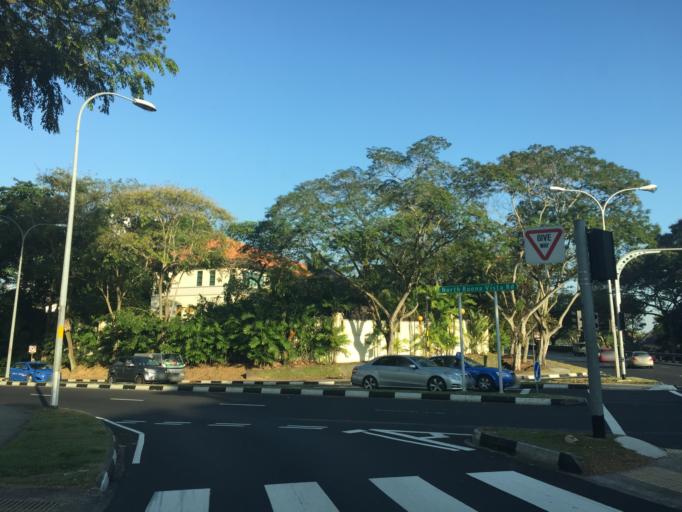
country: SG
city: Singapore
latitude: 1.3132
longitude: 103.7933
